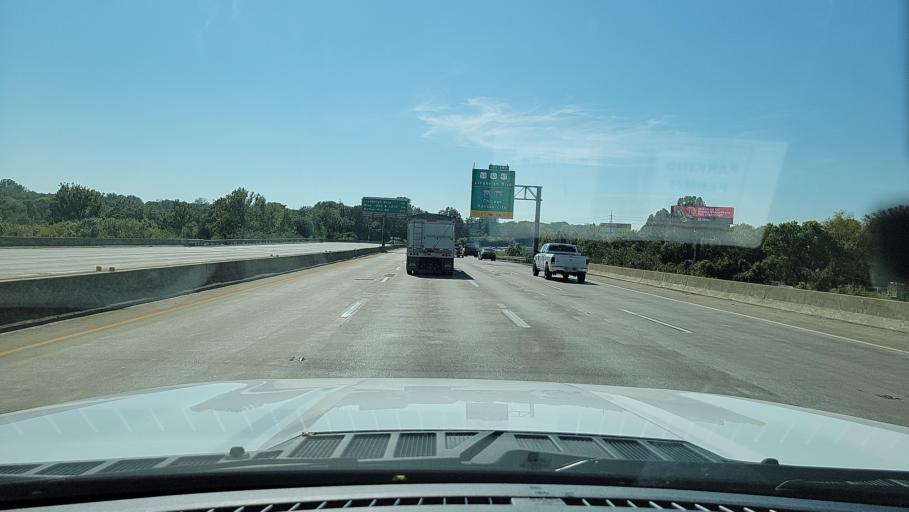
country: US
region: Missouri
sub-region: Saint Louis County
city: Saint George
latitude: 38.5249
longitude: -90.3196
